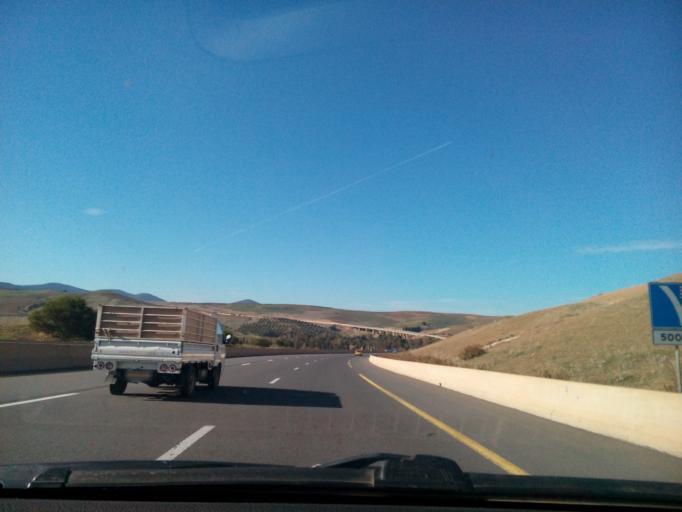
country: DZ
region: Tlemcen
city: Sidi Abdelli
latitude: 35.0379
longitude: -1.0521
